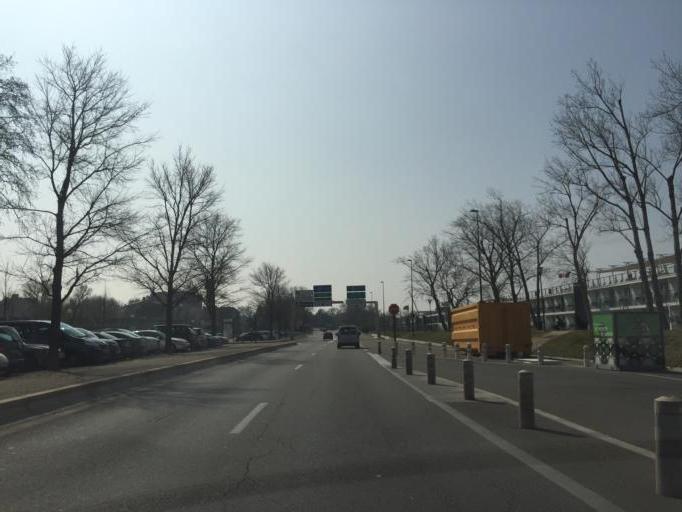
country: FR
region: Provence-Alpes-Cote d'Azur
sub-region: Departement du Vaucluse
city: Avignon
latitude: 43.9487
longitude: 4.7998
